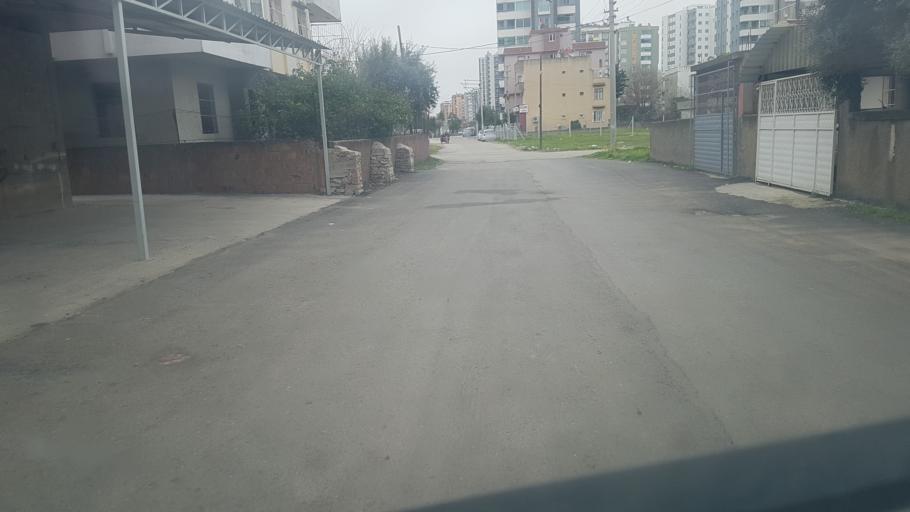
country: TR
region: Adana
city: Seyhan
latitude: 37.0227
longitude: 35.2729
